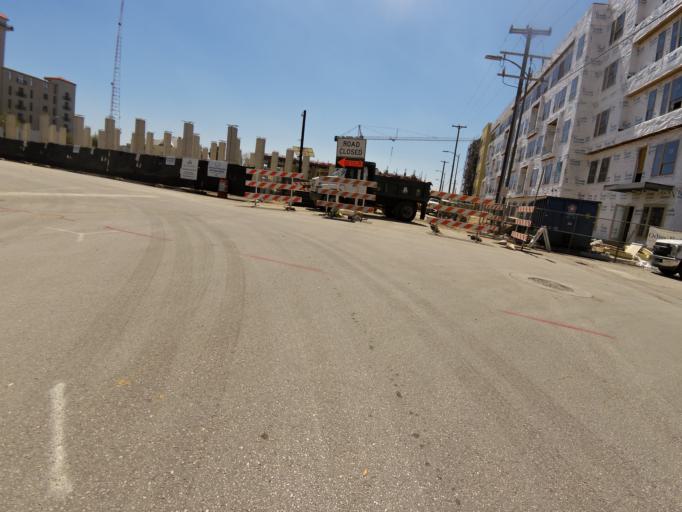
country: US
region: Texas
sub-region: Bexar County
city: San Antonio
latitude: 29.4214
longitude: -98.4946
